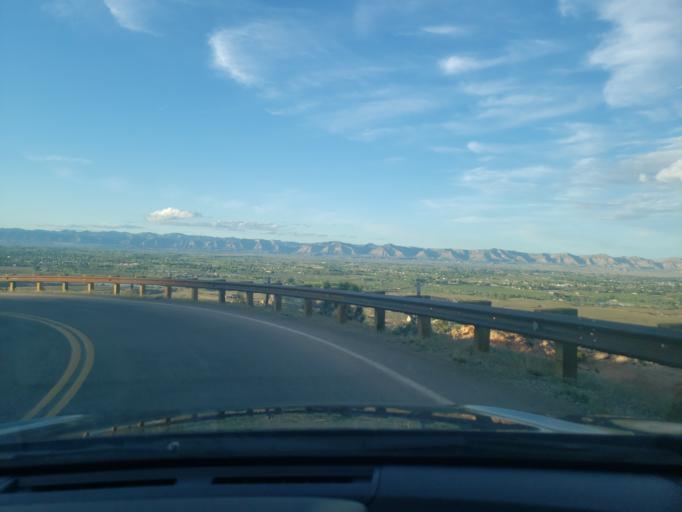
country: US
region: Colorado
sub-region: Mesa County
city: Fruita
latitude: 39.1145
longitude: -108.7246
